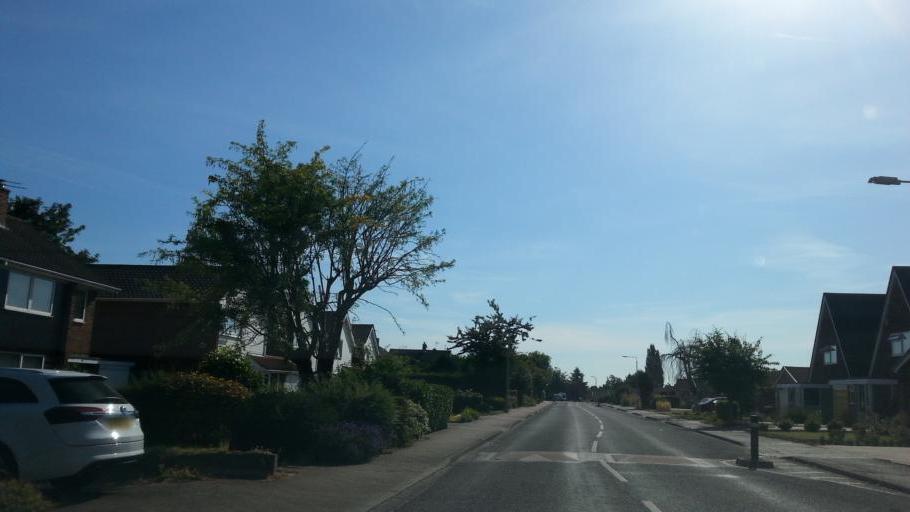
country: GB
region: England
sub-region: Derbyshire
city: Long Eaton
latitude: 52.9181
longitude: -1.2407
